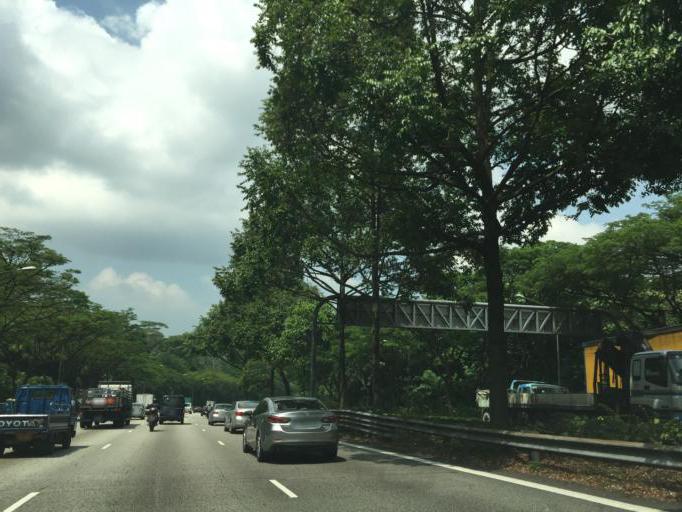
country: SG
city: Singapore
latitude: 1.3298
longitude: 103.8220
